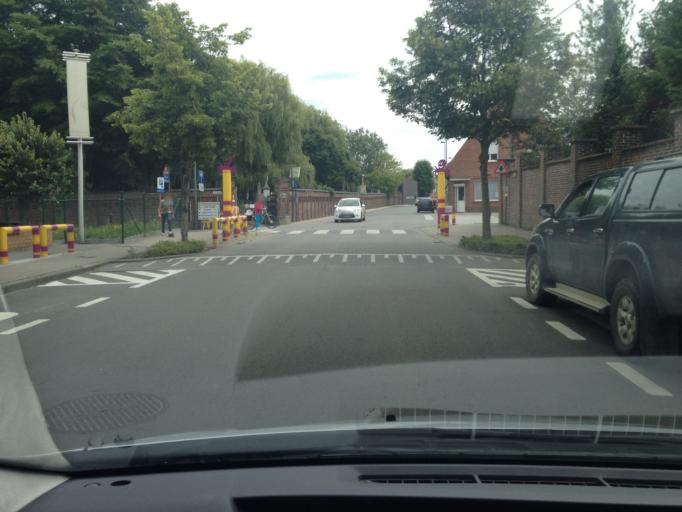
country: BE
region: Flanders
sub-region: Provincie West-Vlaanderen
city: Poperinge
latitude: 50.8523
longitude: 2.7262
